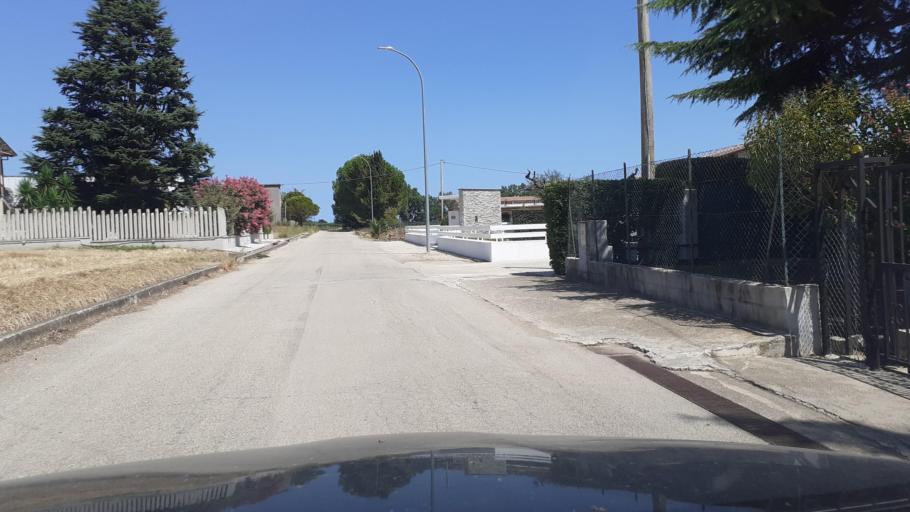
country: IT
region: Abruzzo
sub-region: Provincia di Chieti
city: Santa Maria Imbaro
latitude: 42.2118
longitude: 14.4638
